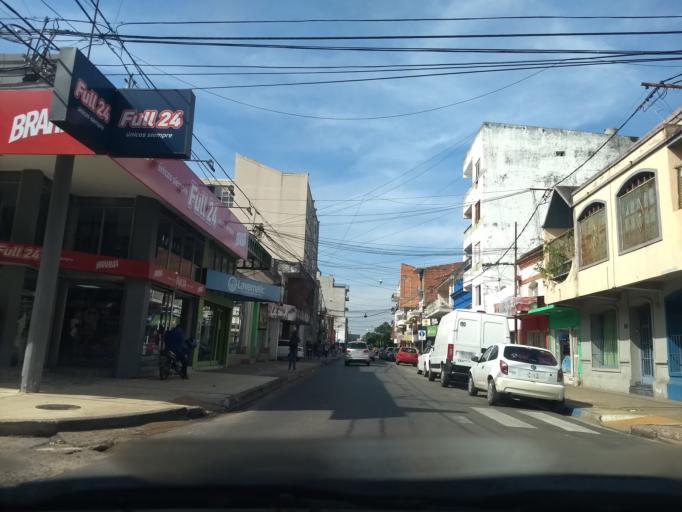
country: AR
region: Corrientes
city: Corrientes
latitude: -27.4699
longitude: -58.8242
